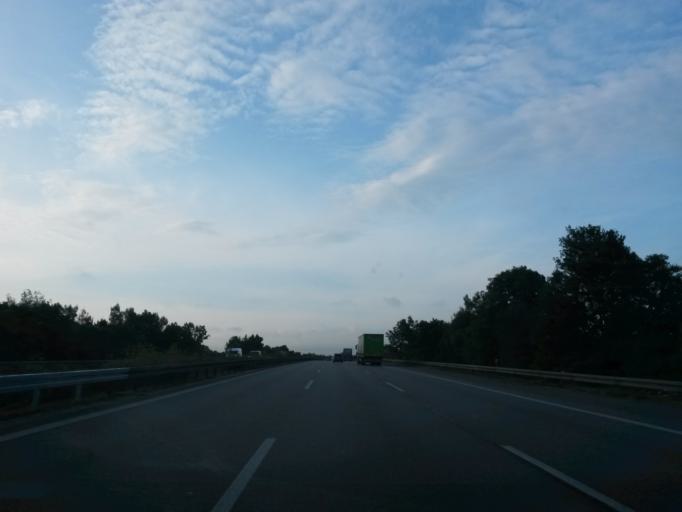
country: DE
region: Bavaria
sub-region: Upper Bavaria
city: Manching
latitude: 48.7296
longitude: 11.4731
